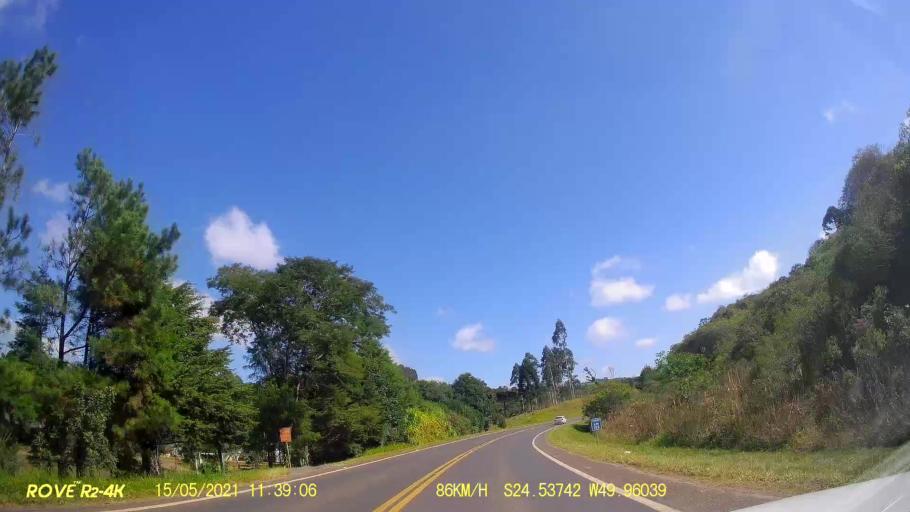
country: BR
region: Parana
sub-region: Pirai Do Sul
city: Pirai do Sul
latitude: -24.5366
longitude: -49.9605
